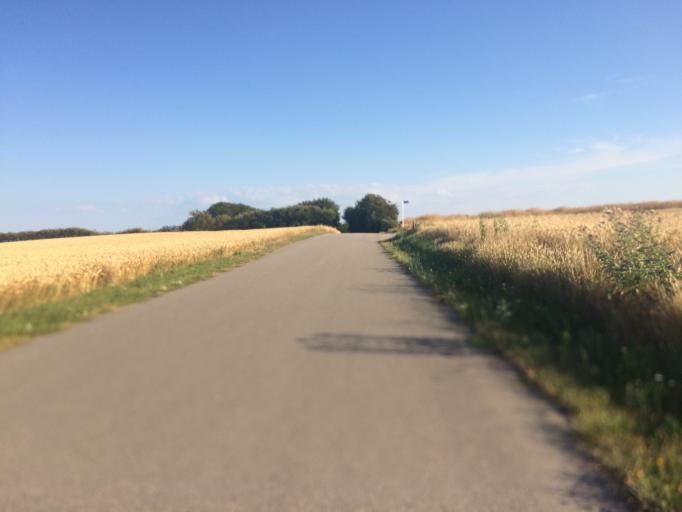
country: DK
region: Central Jutland
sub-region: Holstebro Kommune
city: Vinderup
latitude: 56.5824
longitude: 8.7913
